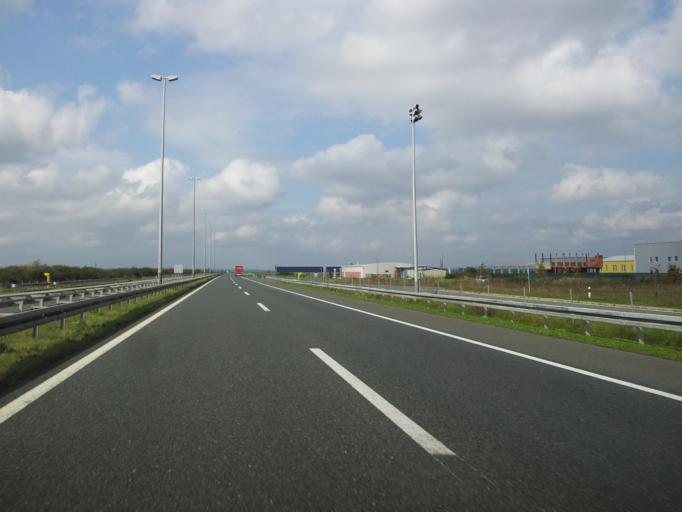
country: HR
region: Brodsko-Posavska
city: Ljupina
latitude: 45.2258
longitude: 17.3799
